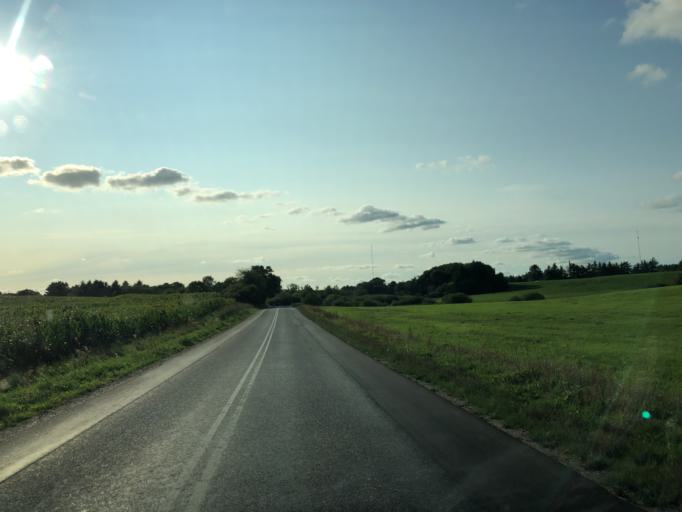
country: DK
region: Central Jutland
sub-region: Viborg Kommune
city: Viborg
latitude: 56.4506
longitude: 9.2918
